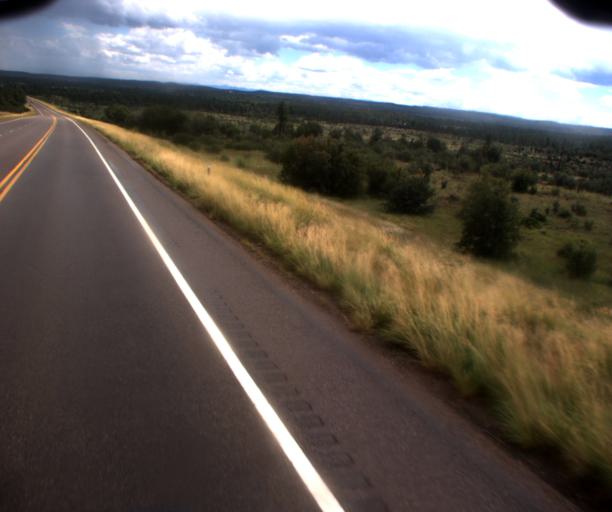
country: US
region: Arizona
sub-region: Navajo County
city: Linden
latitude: 34.3648
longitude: -110.3523
